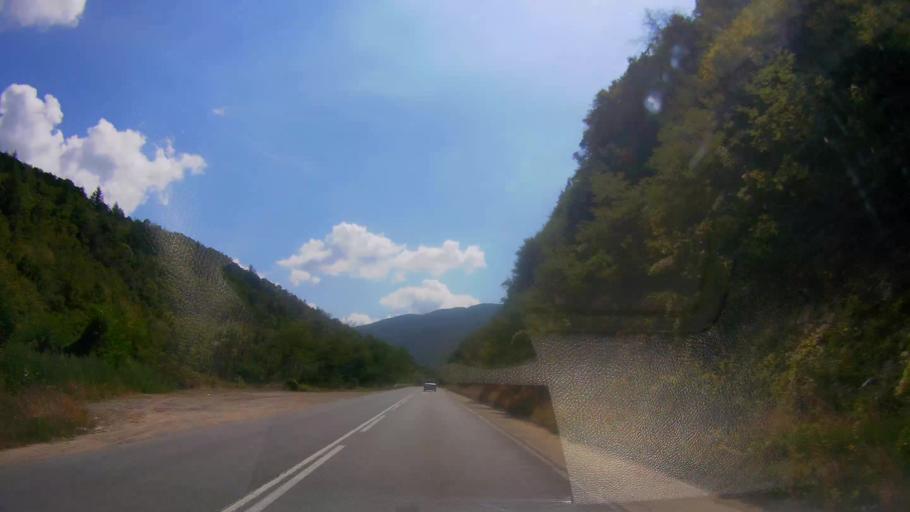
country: BG
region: Stara Zagora
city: Gurkovo
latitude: 42.7244
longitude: 25.7130
